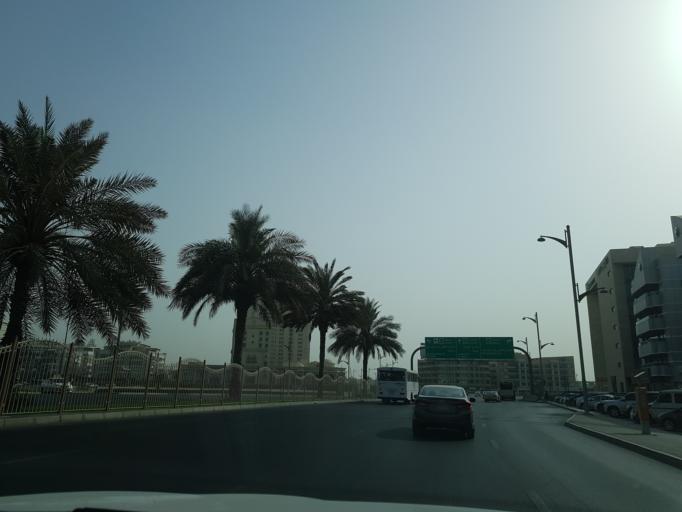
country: AE
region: Ash Shariqah
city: Sharjah
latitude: 25.2410
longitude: 55.2748
